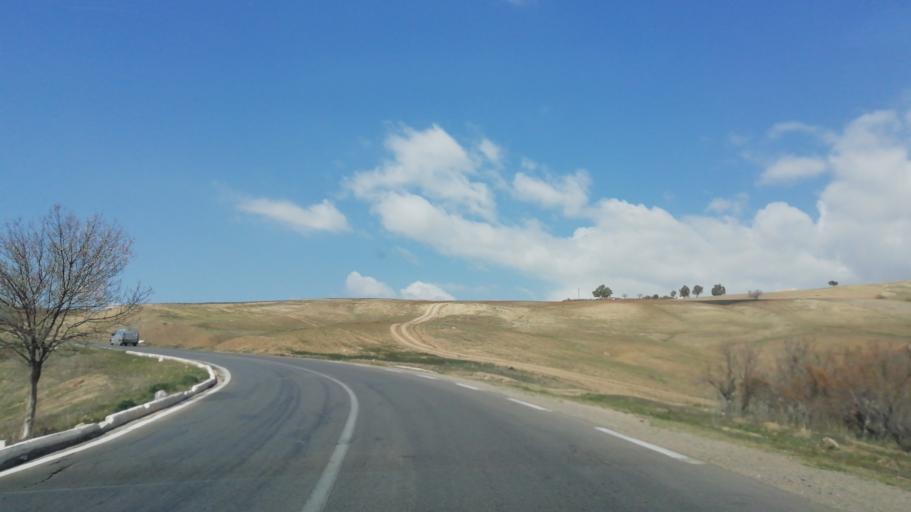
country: DZ
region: Mascara
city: Mascara
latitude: 35.5427
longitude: 0.1121
